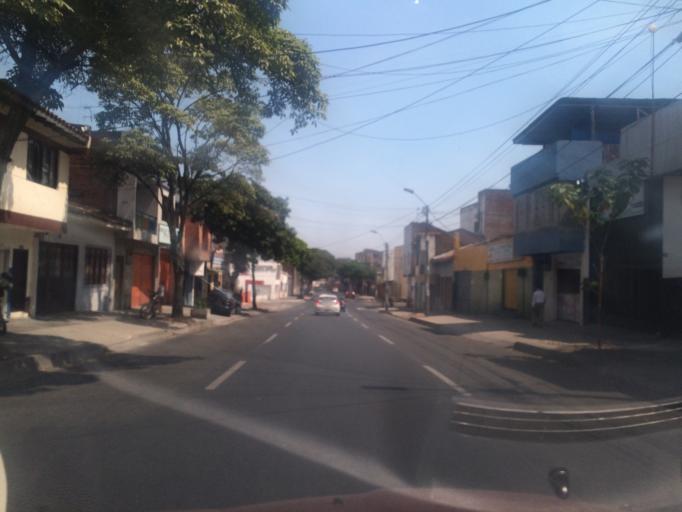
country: CO
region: Valle del Cauca
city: Cali
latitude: 3.4444
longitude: -76.5341
